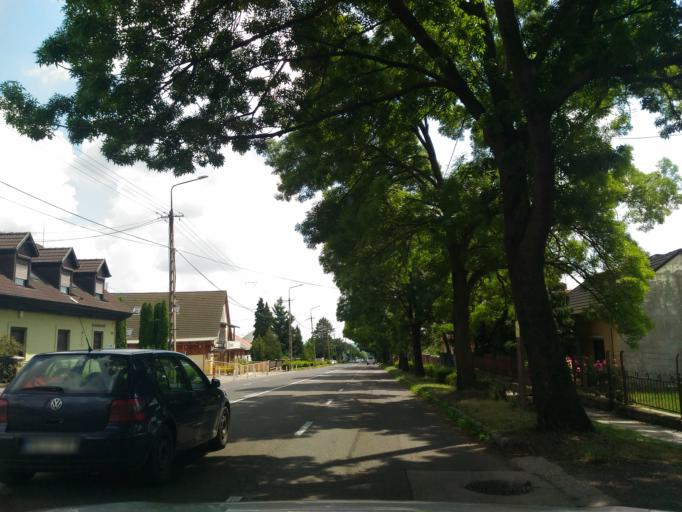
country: HU
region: Baranya
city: Pecs
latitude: 46.1061
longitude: 18.2638
